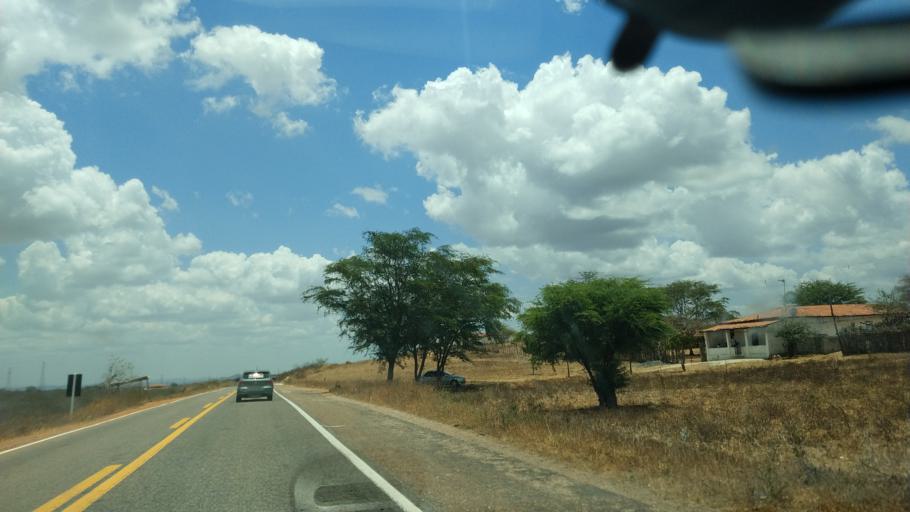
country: BR
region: Rio Grande do Norte
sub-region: Cerro Cora
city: Cerro Cora
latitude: -6.1891
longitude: -36.2490
